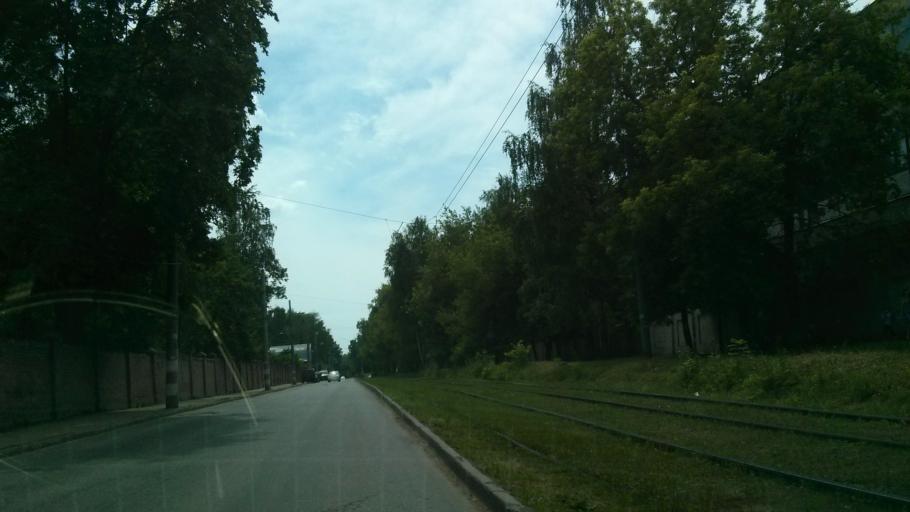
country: RU
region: Nizjnij Novgorod
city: Nizhniy Novgorod
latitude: 56.3015
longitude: 43.9913
